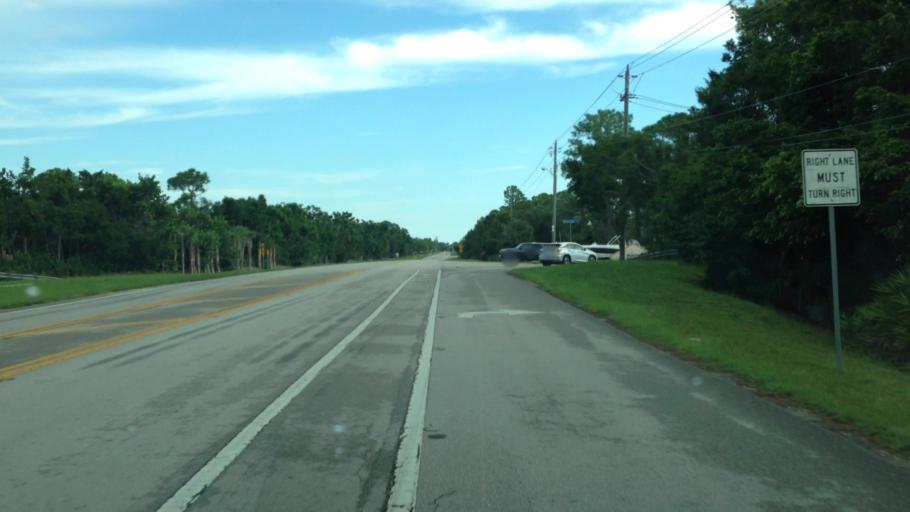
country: US
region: Florida
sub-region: Lee County
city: Bonita Springs
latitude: 26.3156
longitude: -81.8190
